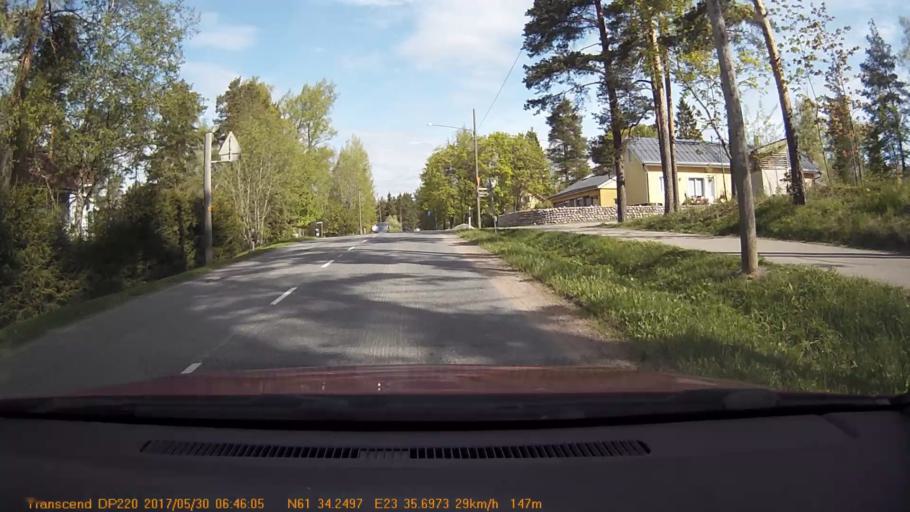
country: FI
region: Pirkanmaa
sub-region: Tampere
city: Yloejaervi
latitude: 61.5707
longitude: 23.5950
